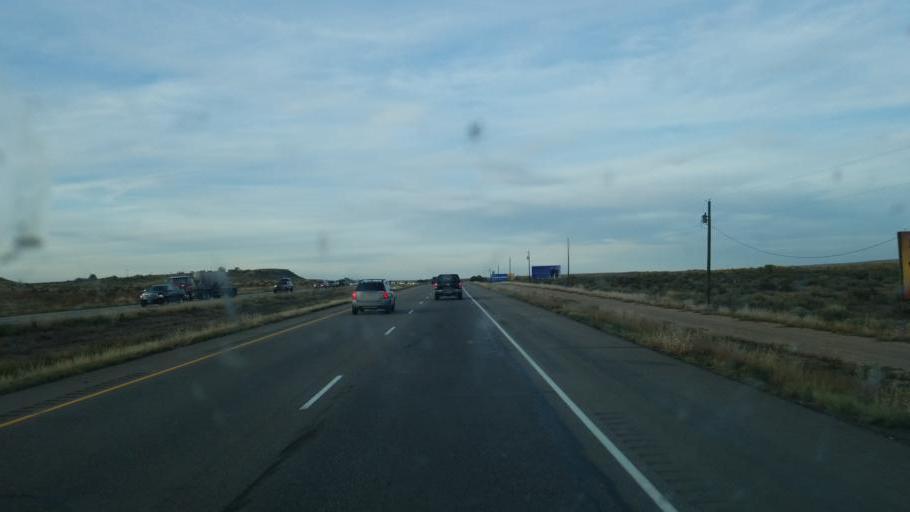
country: US
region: Colorado
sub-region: Pueblo County
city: Pueblo West
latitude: 38.4148
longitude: -104.6117
